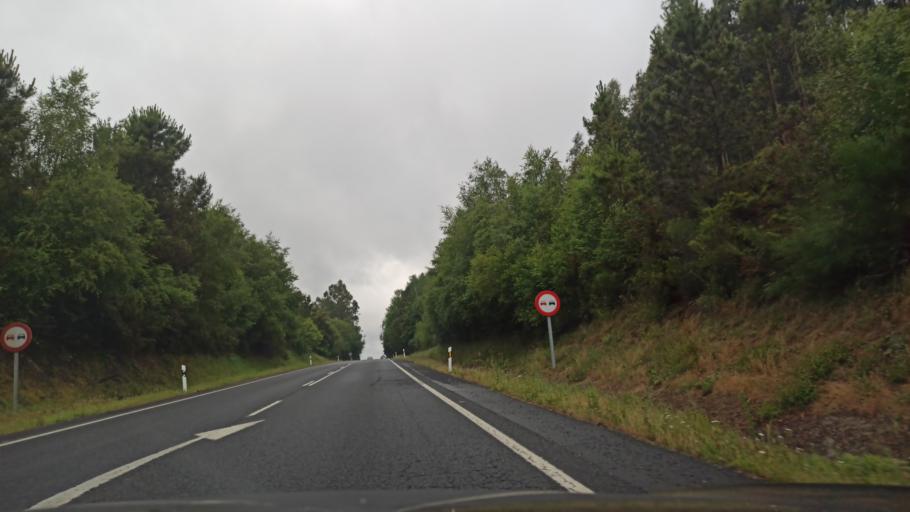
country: ES
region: Galicia
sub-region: Provincia da Coruna
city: Santiso
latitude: 42.7644
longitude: -8.0020
